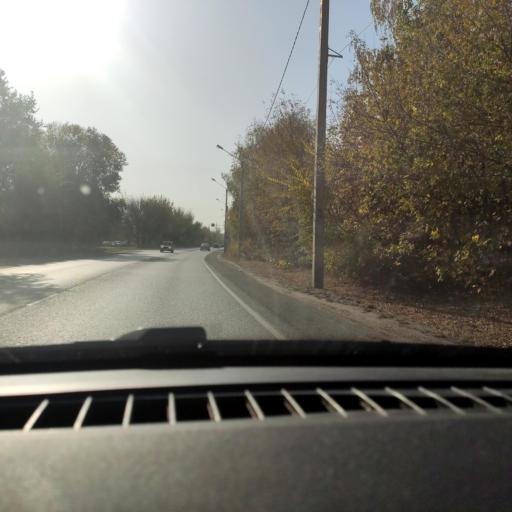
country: RU
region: Voronezj
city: Maslovka
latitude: 51.5867
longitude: 39.1718
